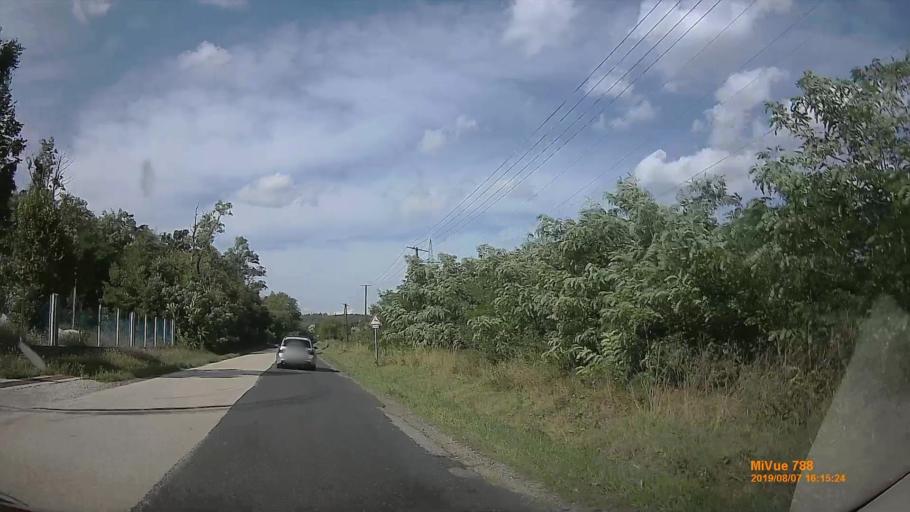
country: HU
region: Zala
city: Gyenesdias
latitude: 46.8002
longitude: 17.2694
